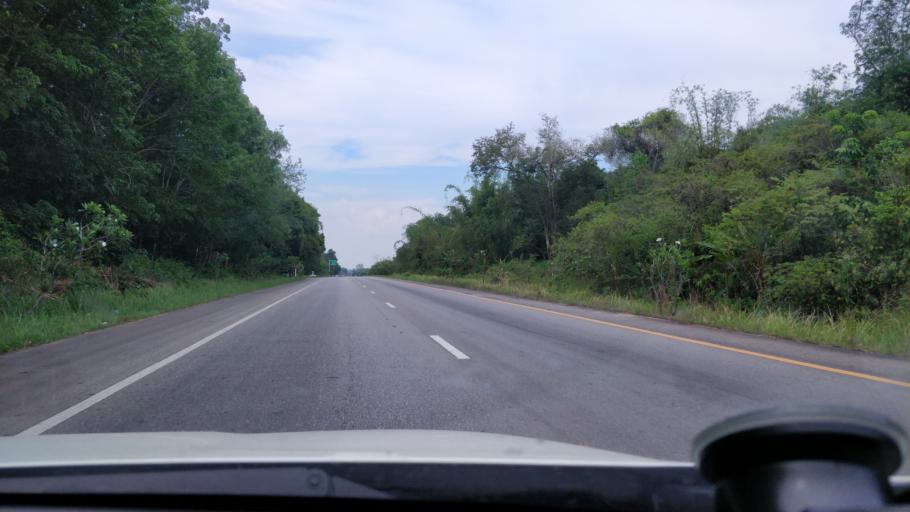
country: TH
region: Surat Thani
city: Khian Sa
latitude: 8.8780
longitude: 99.2085
